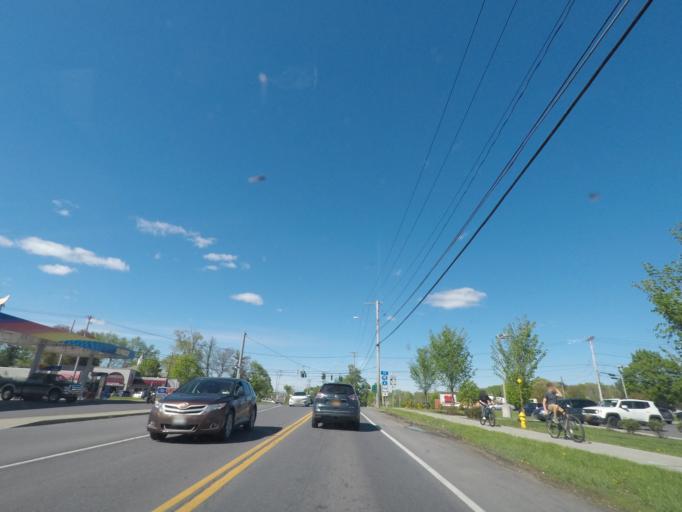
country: US
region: New York
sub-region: Albany County
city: Delmar
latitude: 42.6013
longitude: -73.7923
